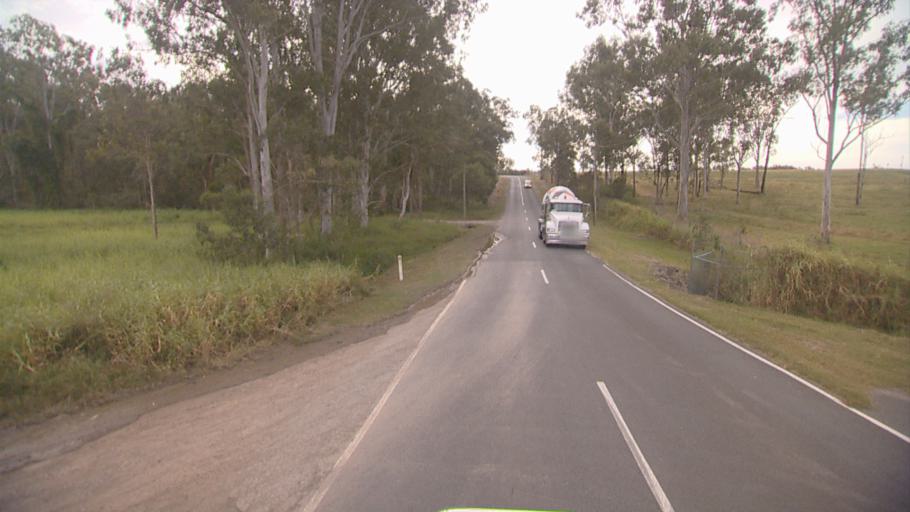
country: AU
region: Queensland
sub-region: Logan
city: Beenleigh
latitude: -27.7181
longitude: 153.1738
